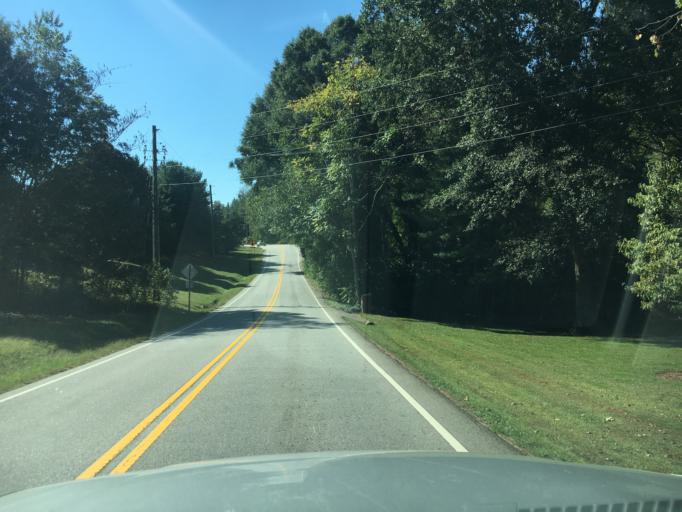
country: US
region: South Carolina
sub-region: Greenville County
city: Taylors
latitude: 34.8735
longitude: -82.2825
